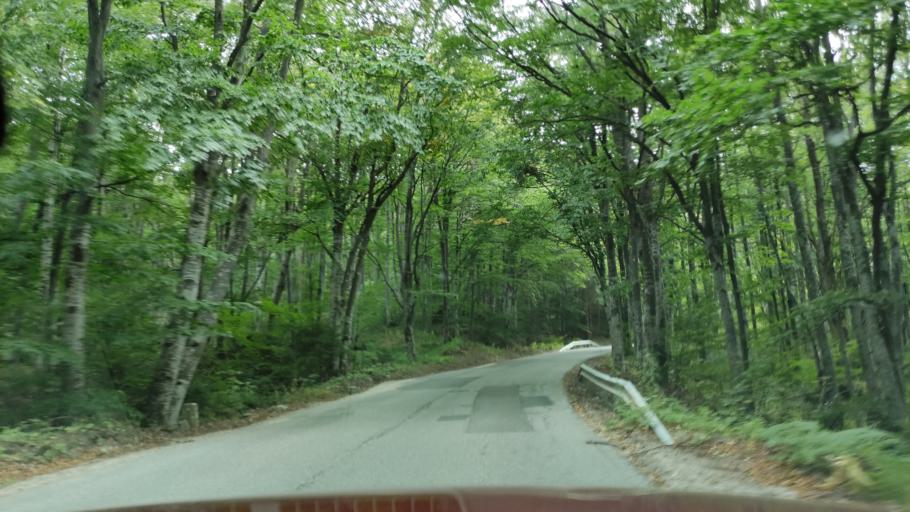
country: BG
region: Sofia-Capital
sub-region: Stolichna Obshtina
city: Sofia
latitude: 42.6265
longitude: 23.2314
